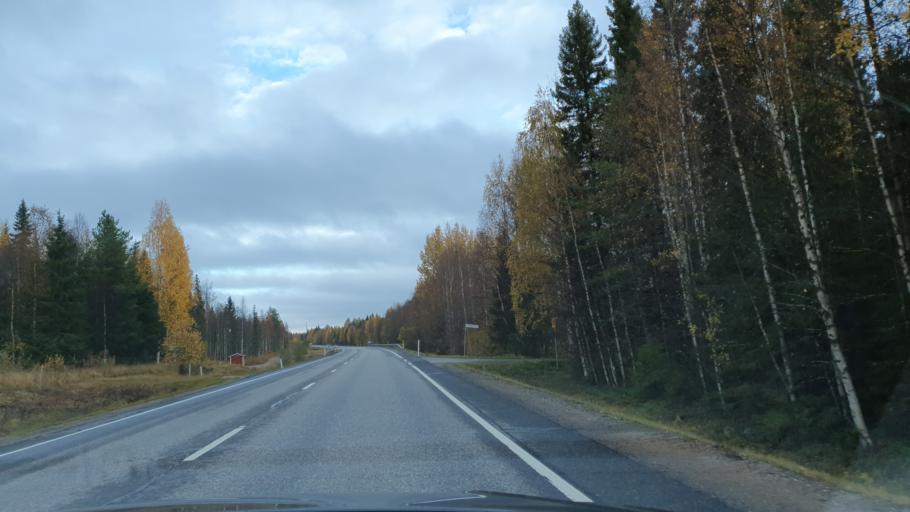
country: FI
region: Lapland
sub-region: Rovaniemi
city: Rovaniemi
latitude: 66.5711
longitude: 25.6350
